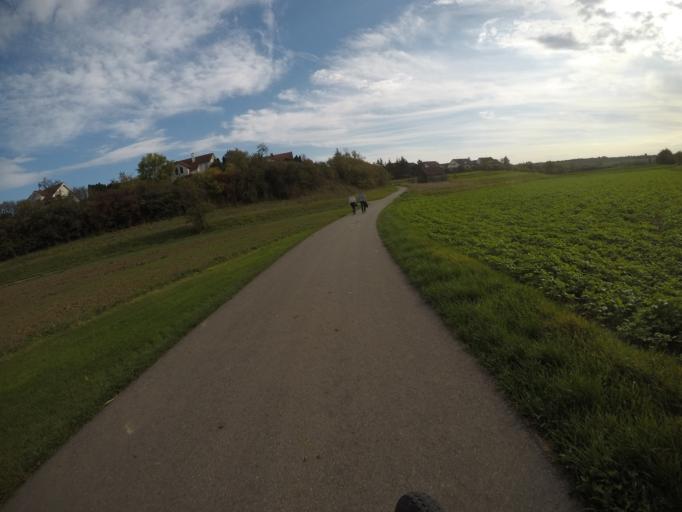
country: DE
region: Baden-Wuerttemberg
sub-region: Regierungsbezirk Stuttgart
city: Herrenberg
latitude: 48.5801
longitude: 8.8740
